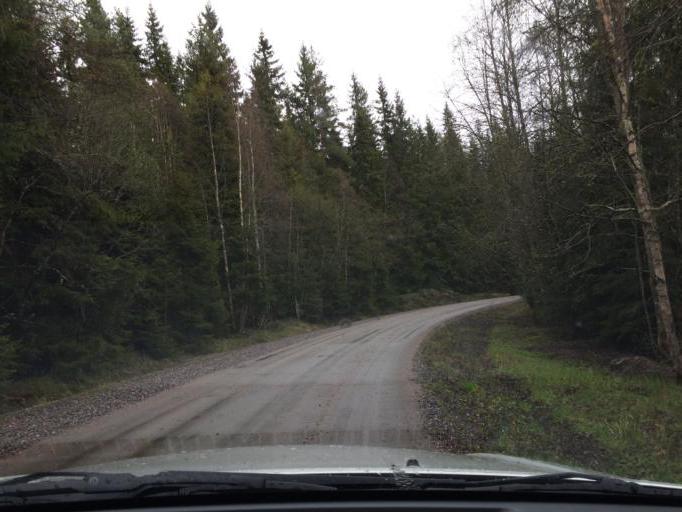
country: SE
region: Dalarna
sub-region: Ludvika Kommun
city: Abborrberget
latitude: 60.0241
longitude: 14.6064
